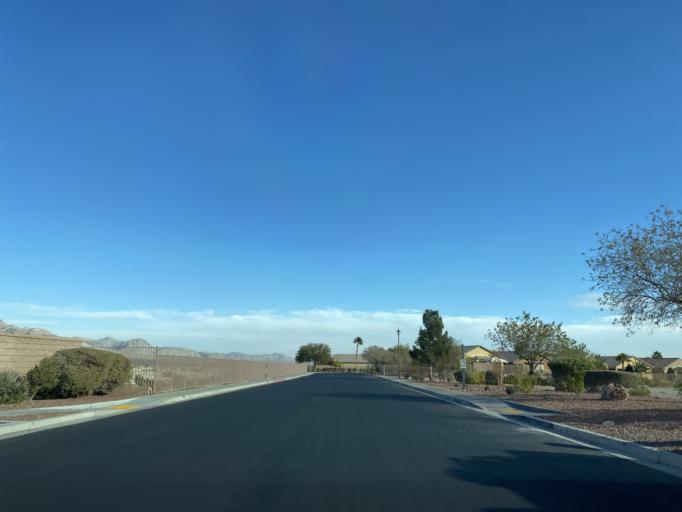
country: US
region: Nevada
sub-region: Clark County
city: North Las Vegas
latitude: 36.3211
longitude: -115.2456
